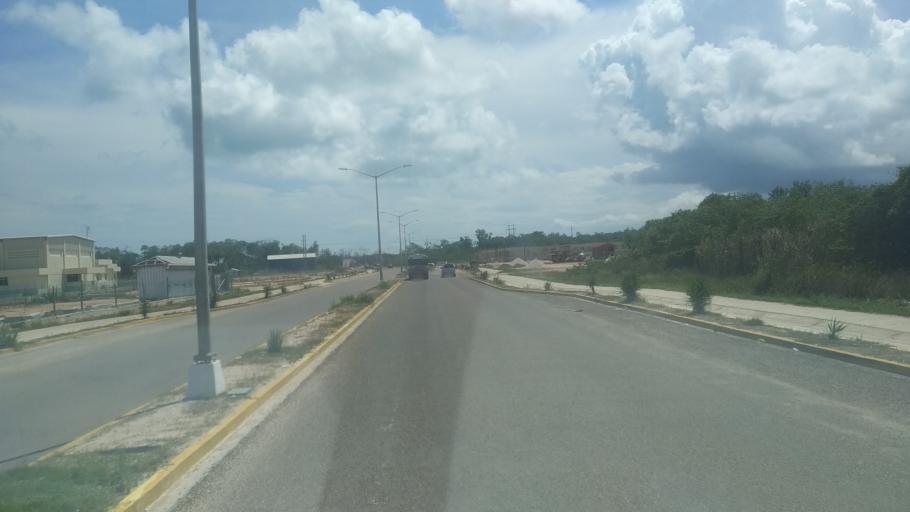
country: BZ
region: Belize
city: Belize City
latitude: 17.5061
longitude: -88.2217
